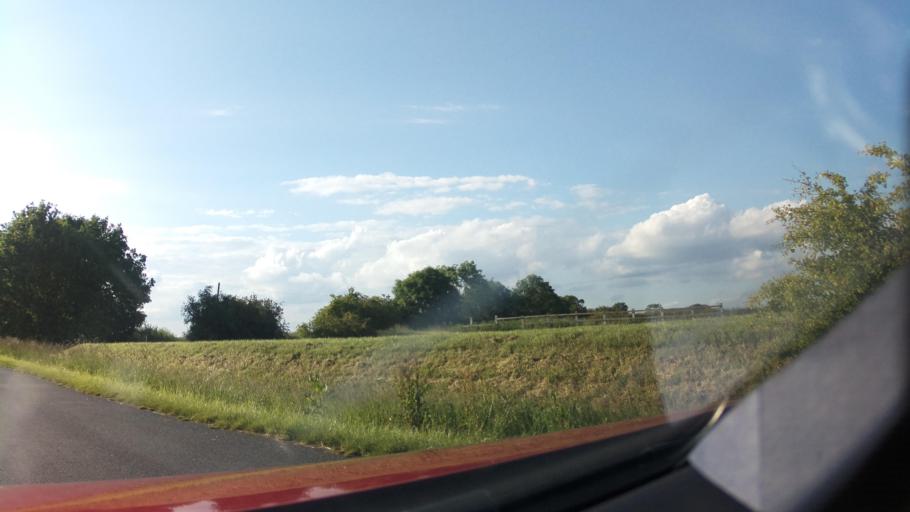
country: GB
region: England
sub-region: Lincolnshire
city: Navenby
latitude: 53.1127
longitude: -0.5989
